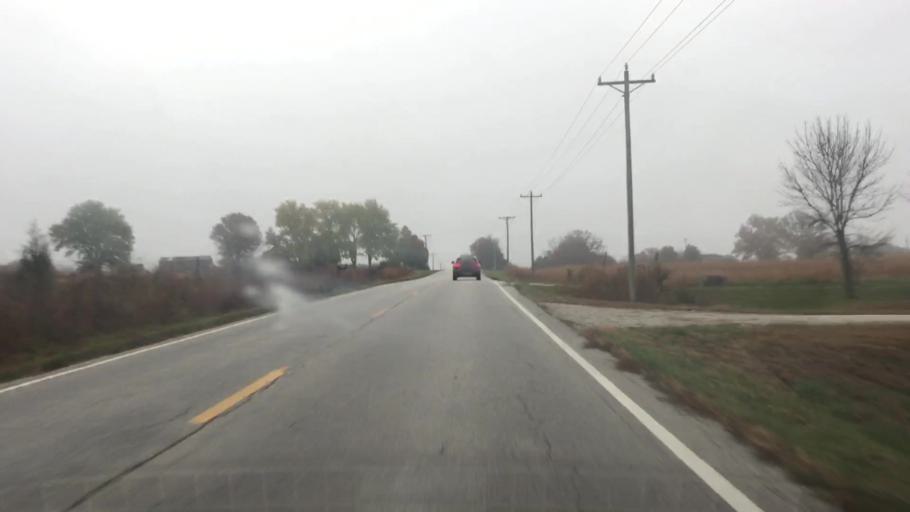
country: US
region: Missouri
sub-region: Callaway County
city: Fulton
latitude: 38.8738
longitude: -92.0478
